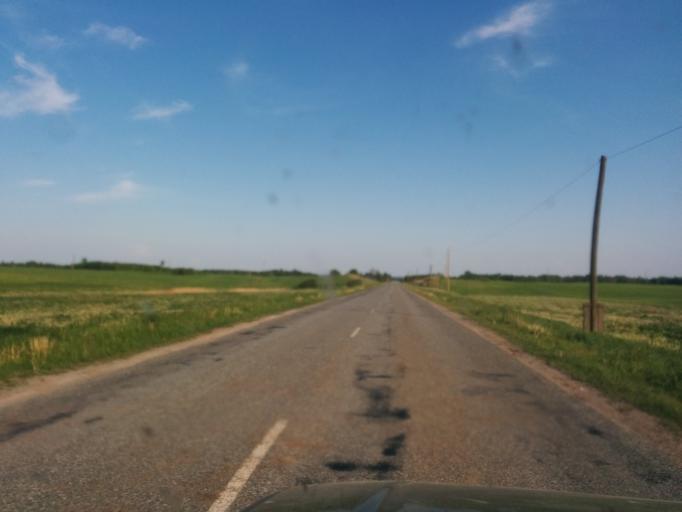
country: LV
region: Talsu Rajons
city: Valdemarpils
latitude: 57.3357
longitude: 22.5120
